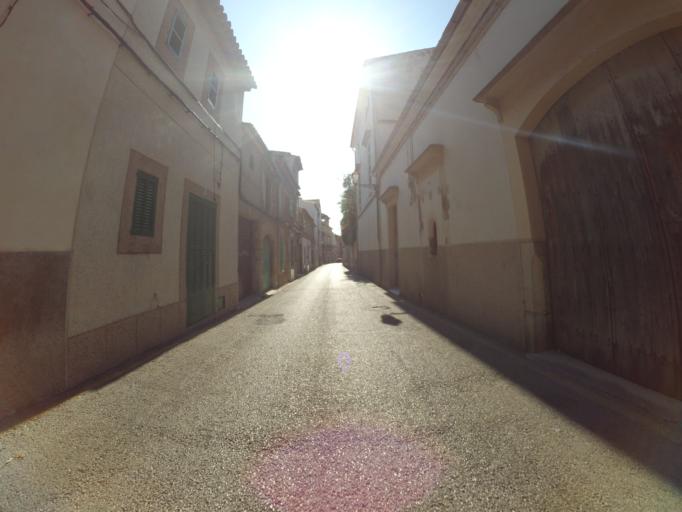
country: ES
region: Balearic Islands
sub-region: Illes Balears
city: Arta
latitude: 39.6958
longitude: 3.3484
